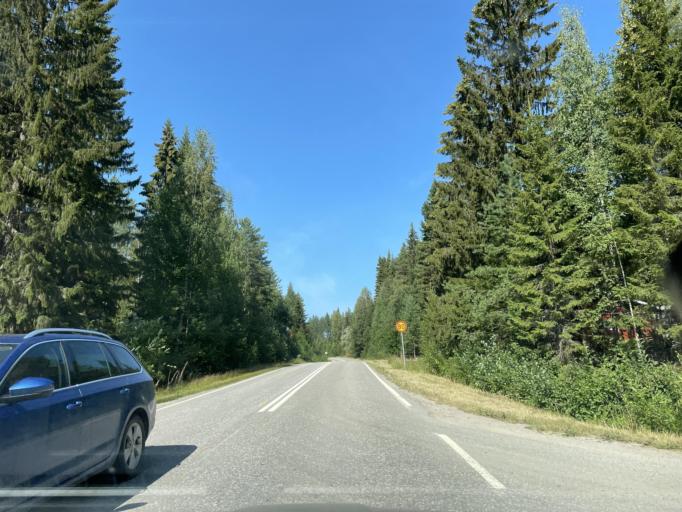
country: FI
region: Central Finland
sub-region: Saarijaervi-Viitasaari
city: Pihtipudas
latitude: 63.3628
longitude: 25.7424
